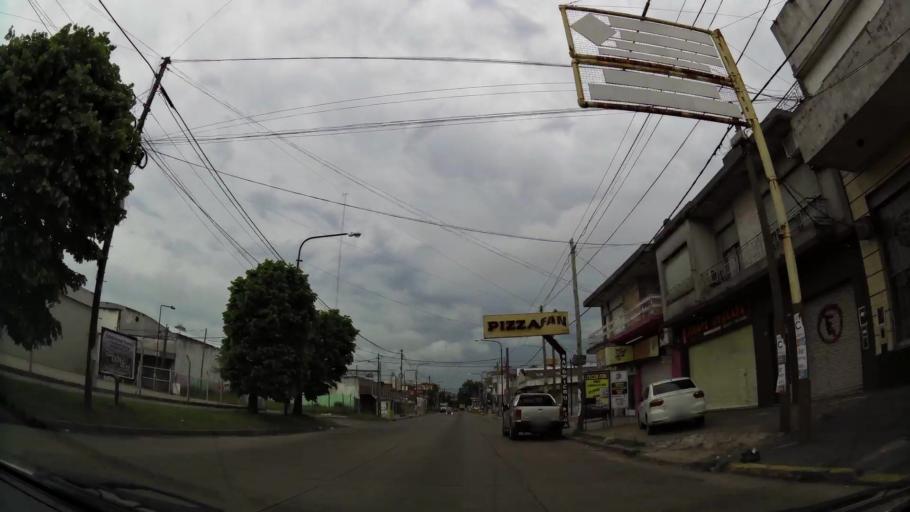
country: AR
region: Buenos Aires
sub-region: Partido de Quilmes
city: Quilmes
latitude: -34.7413
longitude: -58.2877
